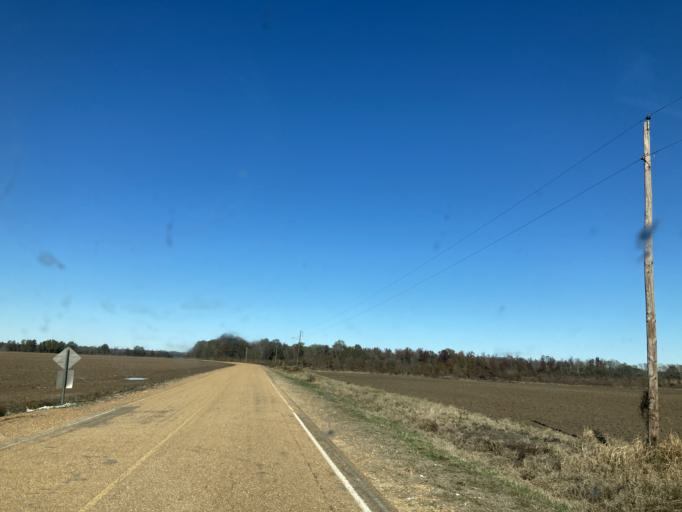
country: US
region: Mississippi
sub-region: Yazoo County
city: Yazoo City
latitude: 32.7424
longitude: -90.6344
